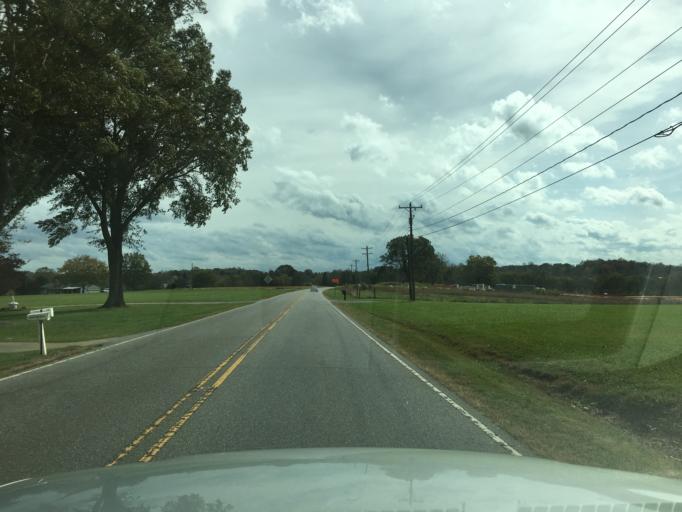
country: US
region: North Carolina
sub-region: Catawba County
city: Newton
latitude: 35.6879
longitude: -81.2796
